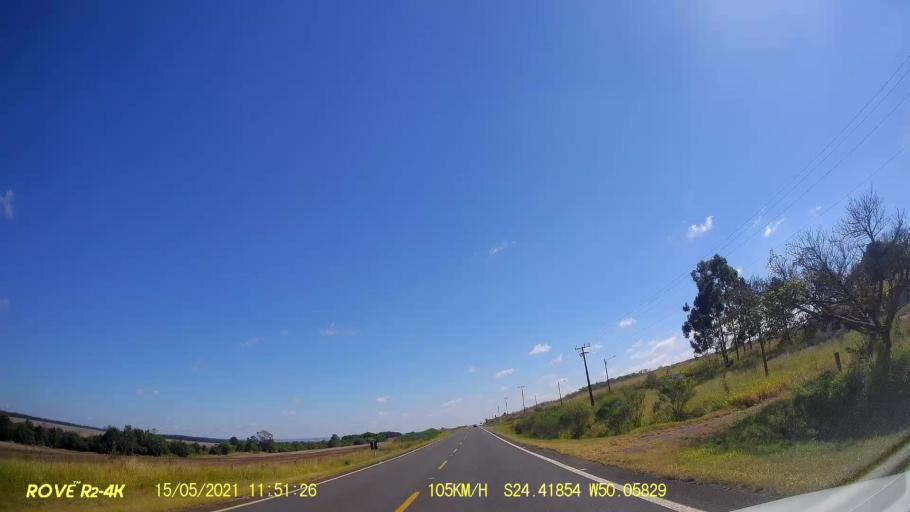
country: BR
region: Parana
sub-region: Pirai Do Sul
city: Pirai do Sul
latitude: -24.4186
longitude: -50.0583
